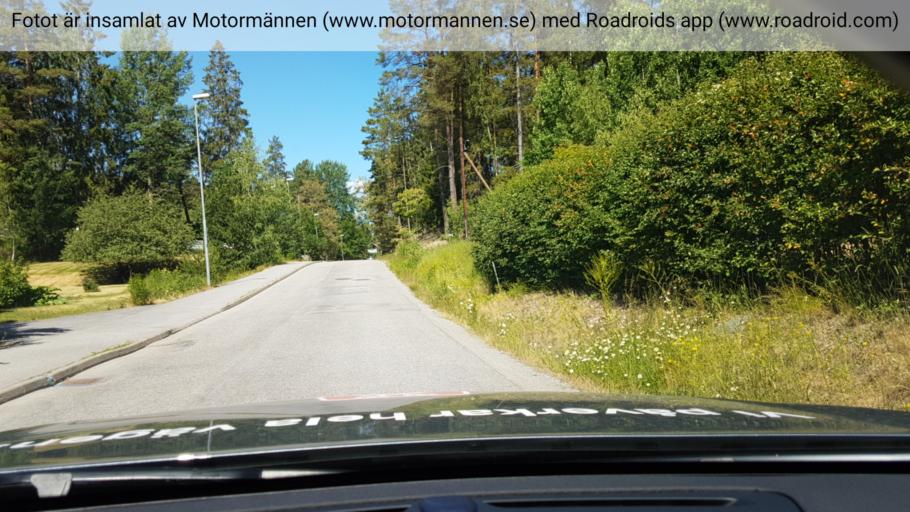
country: SE
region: Stockholm
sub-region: Nacka Kommun
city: Fisksatra
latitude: 59.2499
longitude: 18.2781
